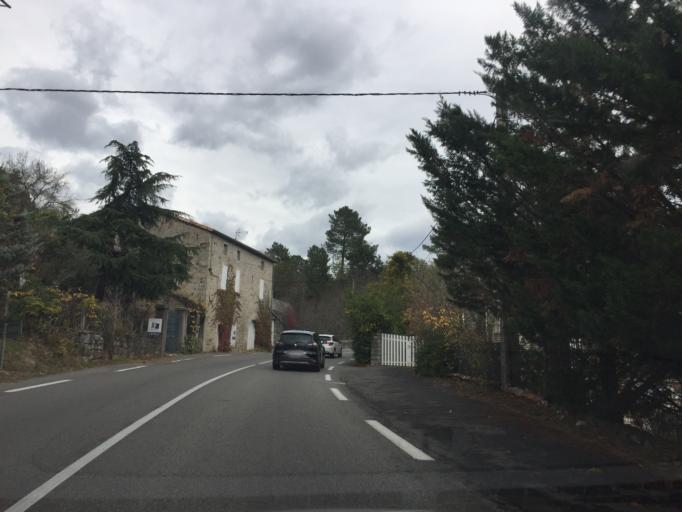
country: FR
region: Rhone-Alpes
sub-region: Departement de l'Ardeche
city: Lablachere
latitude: 44.4502
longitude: 4.2111
